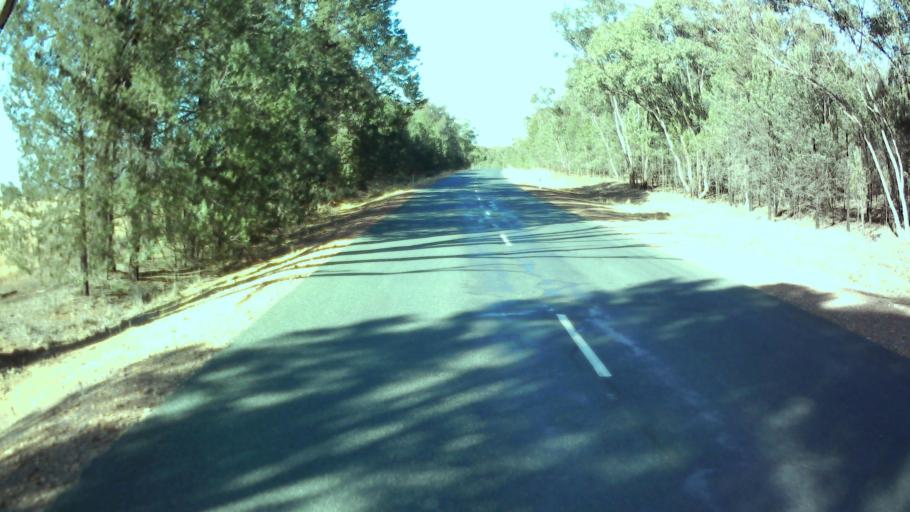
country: AU
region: New South Wales
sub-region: Weddin
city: Grenfell
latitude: -34.0122
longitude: 148.1158
